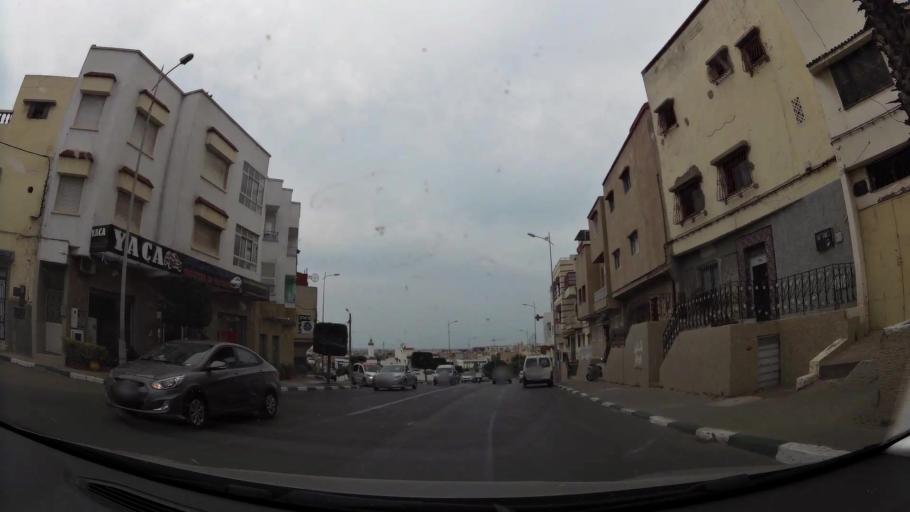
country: MA
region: Rabat-Sale-Zemmour-Zaer
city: Sale
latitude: 34.0275
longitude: -6.8069
